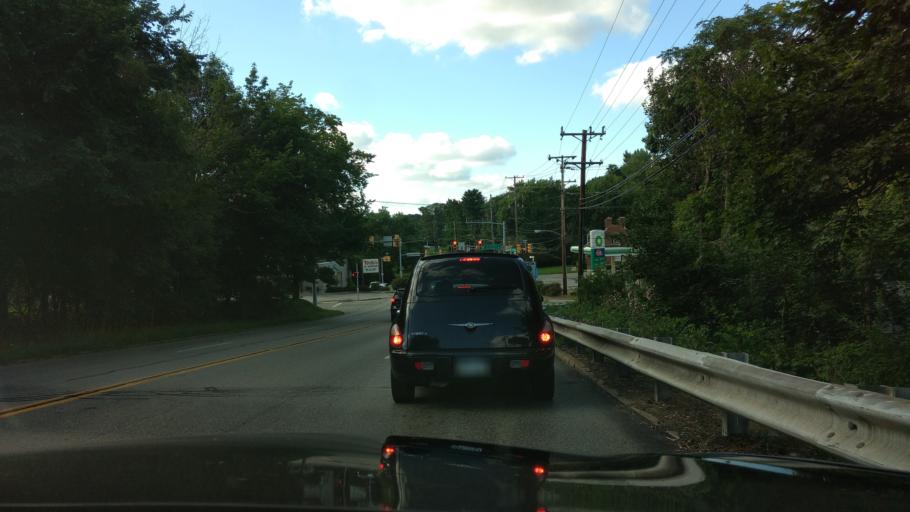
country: US
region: Pennsylvania
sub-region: Allegheny County
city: West View
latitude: 40.5440
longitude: -80.0359
